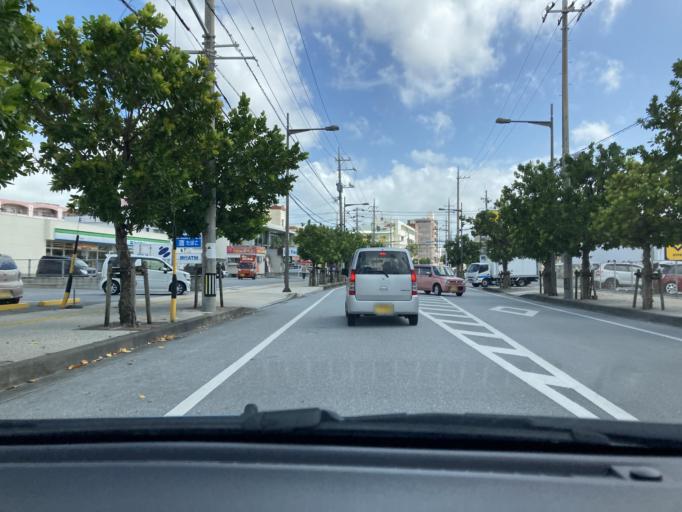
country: JP
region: Okinawa
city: Ginowan
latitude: 26.2738
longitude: 127.7296
